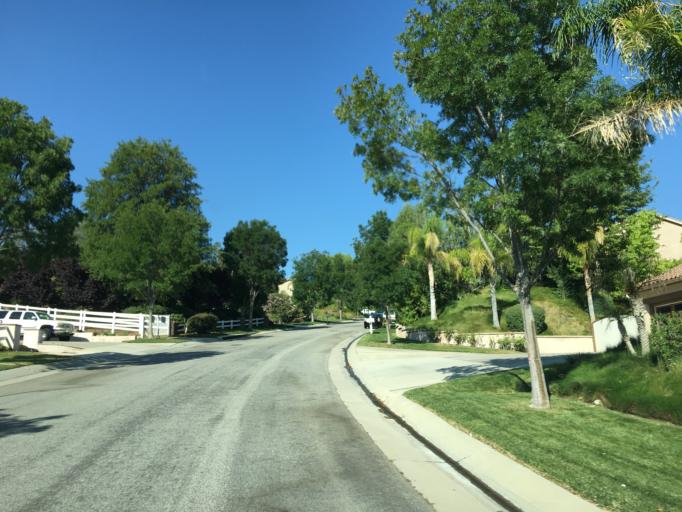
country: US
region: California
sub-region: Los Angeles County
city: Val Verde
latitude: 34.4638
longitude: -118.6673
